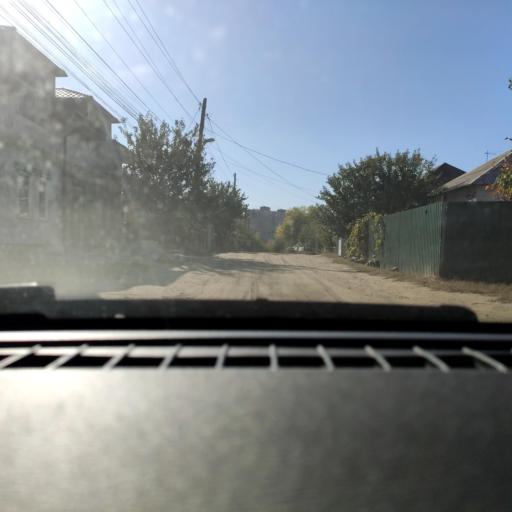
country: RU
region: Voronezj
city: Voronezh
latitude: 51.6656
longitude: 39.2864
